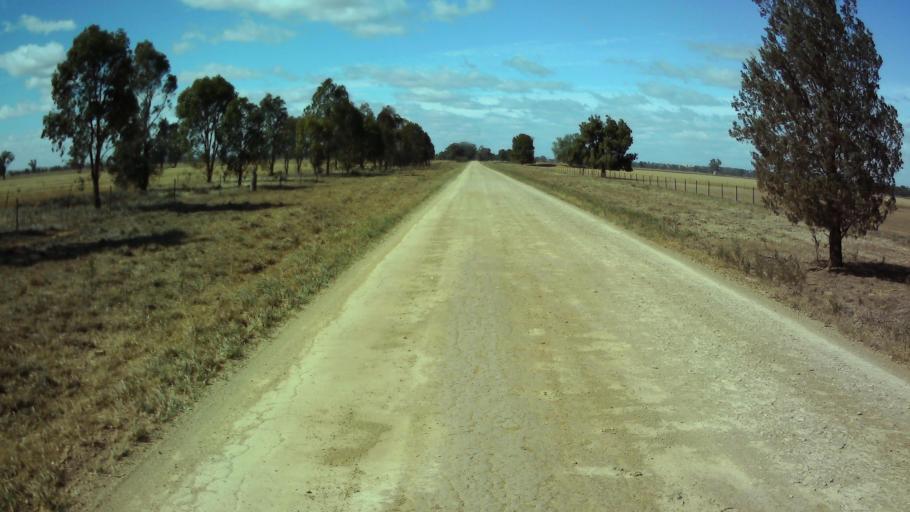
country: AU
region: New South Wales
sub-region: Weddin
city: Grenfell
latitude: -34.0194
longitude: 148.3193
